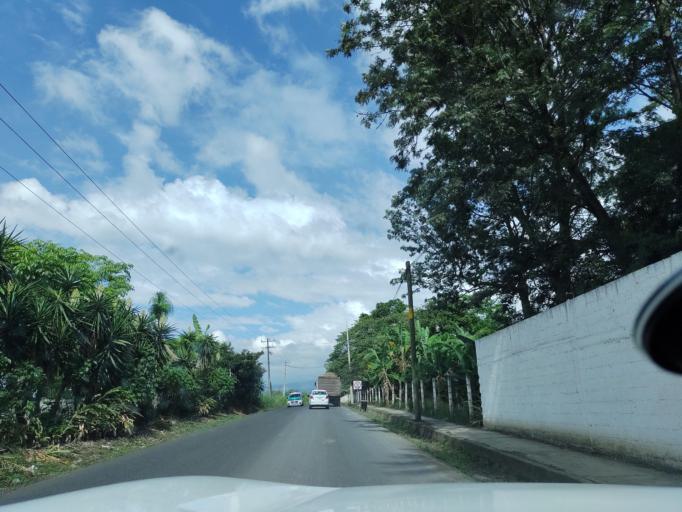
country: MX
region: Veracruz
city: Coatepec
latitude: 19.4814
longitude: -96.9367
